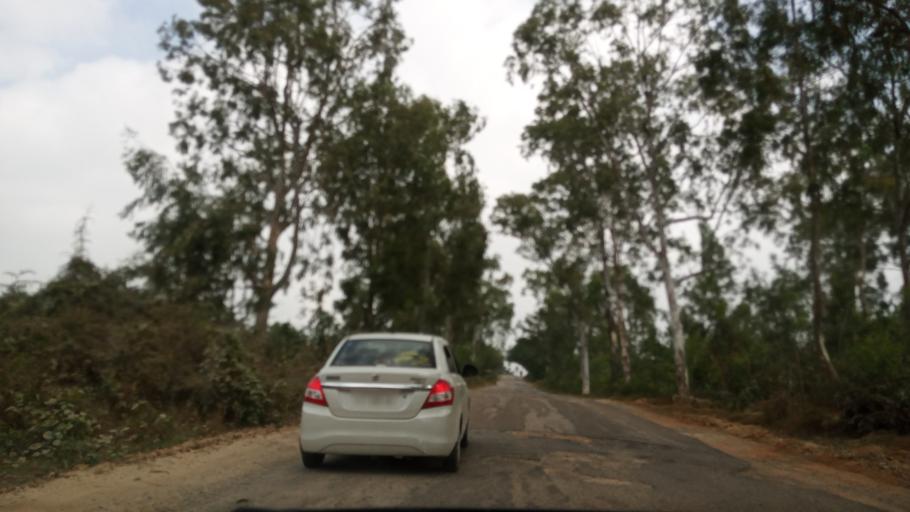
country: IN
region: Andhra Pradesh
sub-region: Chittoor
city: Madanapalle
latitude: 13.5087
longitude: 78.3358
